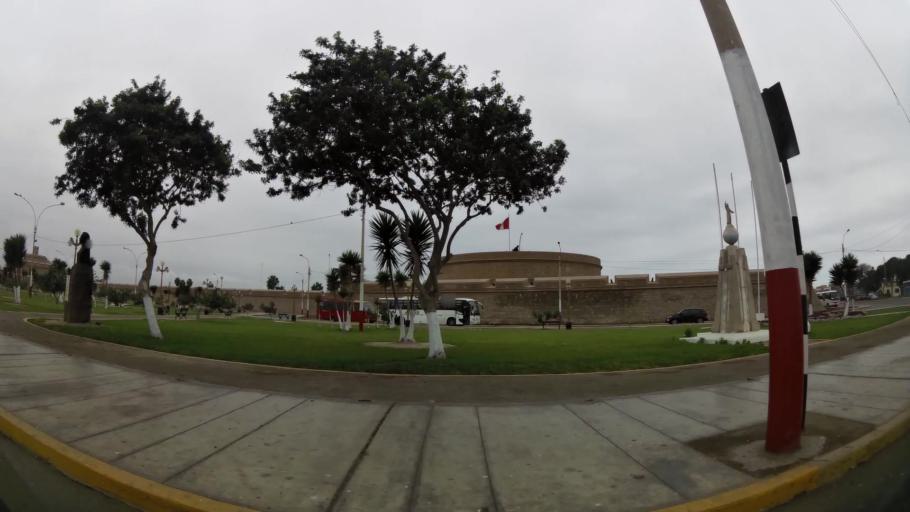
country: PE
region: Callao
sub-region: Callao
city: Callao
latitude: -12.0618
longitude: -77.1510
